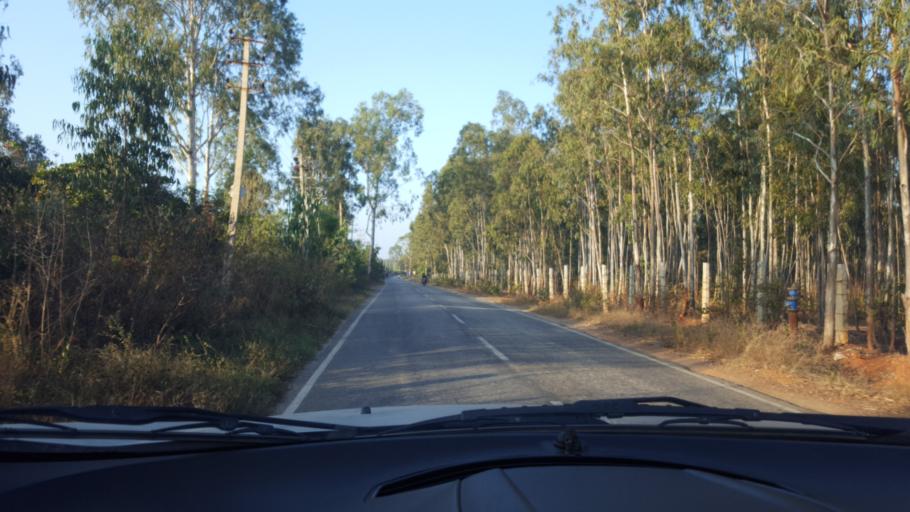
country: IN
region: Karnataka
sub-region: Bangalore Urban
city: Yelahanka
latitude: 13.1806
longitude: 77.5994
